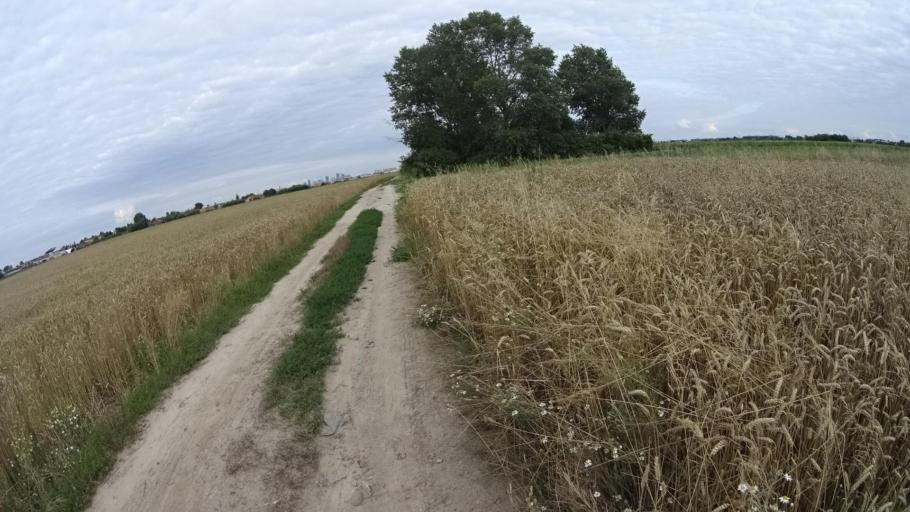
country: PL
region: Masovian Voivodeship
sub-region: Powiat warszawski zachodni
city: Babice
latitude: 52.2401
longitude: 20.8618
